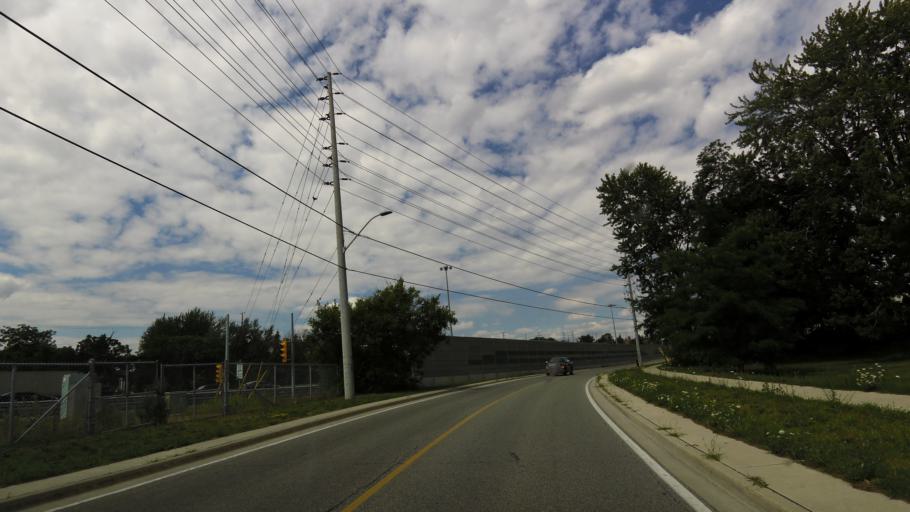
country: CA
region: Ontario
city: Mississauga
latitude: 43.5691
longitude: -79.5978
